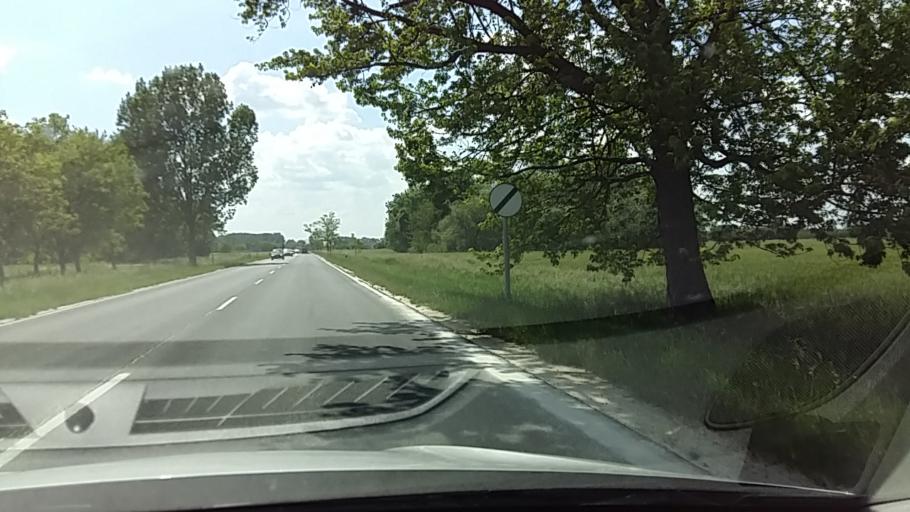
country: HU
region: Gyor-Moson-Sopron
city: Farad
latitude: 47.5929
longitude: 17.1335
